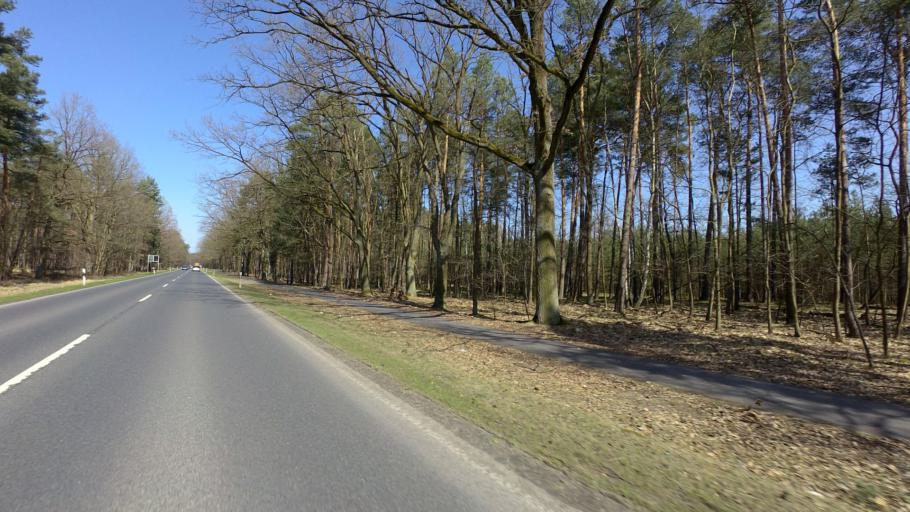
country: DE
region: Brandenburg
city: Oranienburg
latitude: 52.7838
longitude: 13.2389
